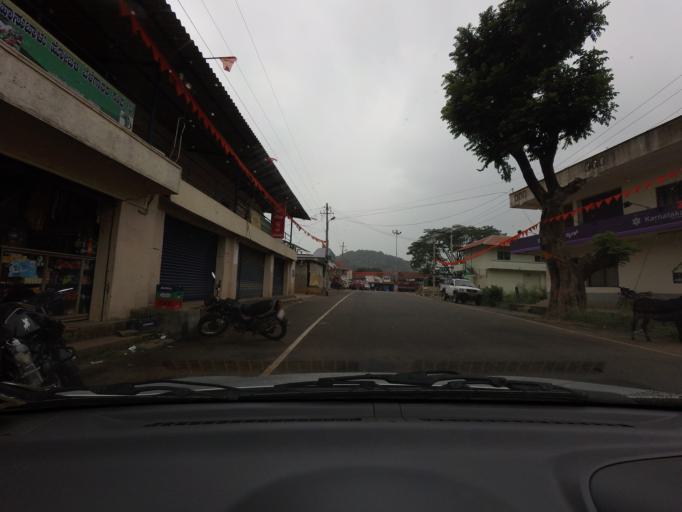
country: IN
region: Karnataka
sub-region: Hassan
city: Sakleshpur
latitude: 13.0042
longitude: 75.6976
